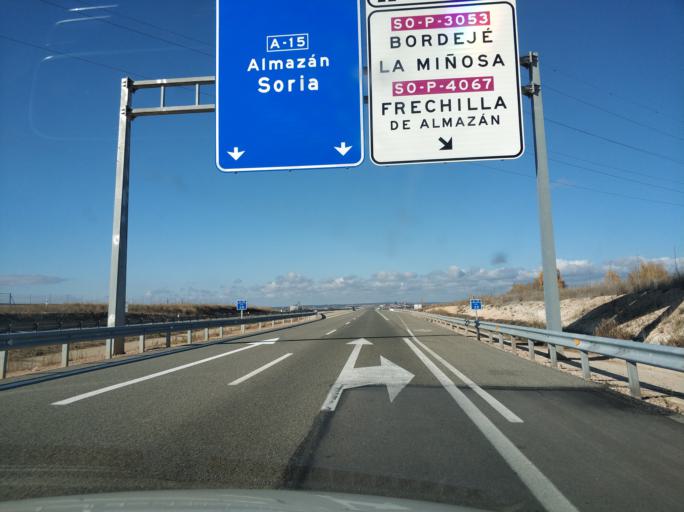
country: ES
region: Castille and Leon
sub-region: Provincia de Soria
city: Frechilla de Almazan
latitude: 41.4425
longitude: -2.5032
